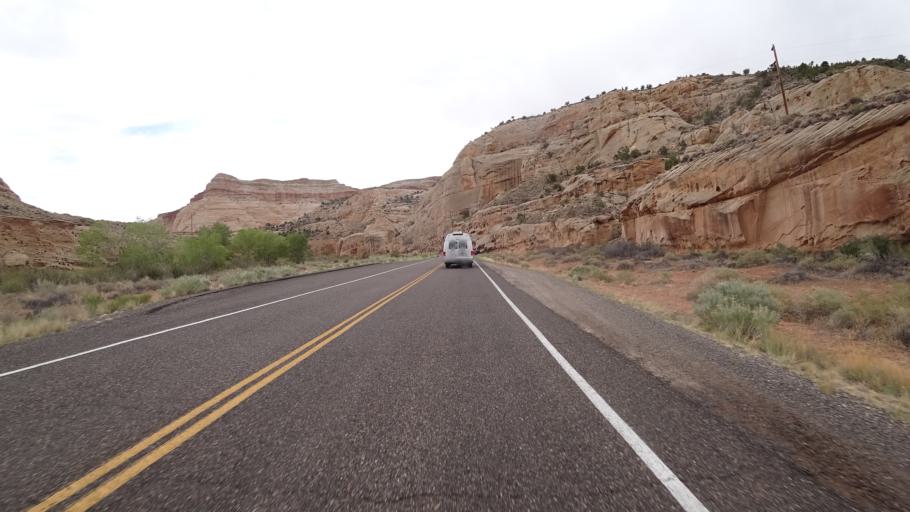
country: US
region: Utah
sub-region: Wayne County
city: Loa
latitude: 38.2824
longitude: -111.1760
